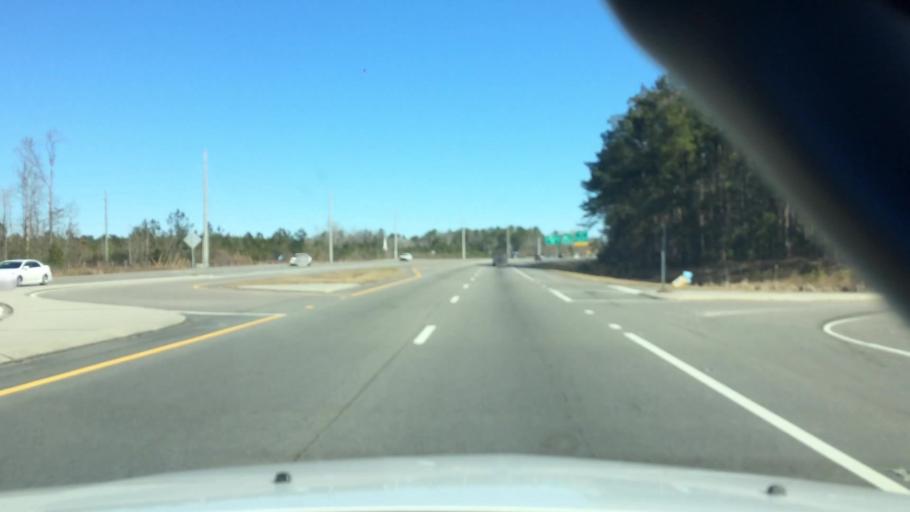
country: US
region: North Carolina
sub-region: Brunswick County
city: Leland
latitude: 34.1751
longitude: -78.0867
